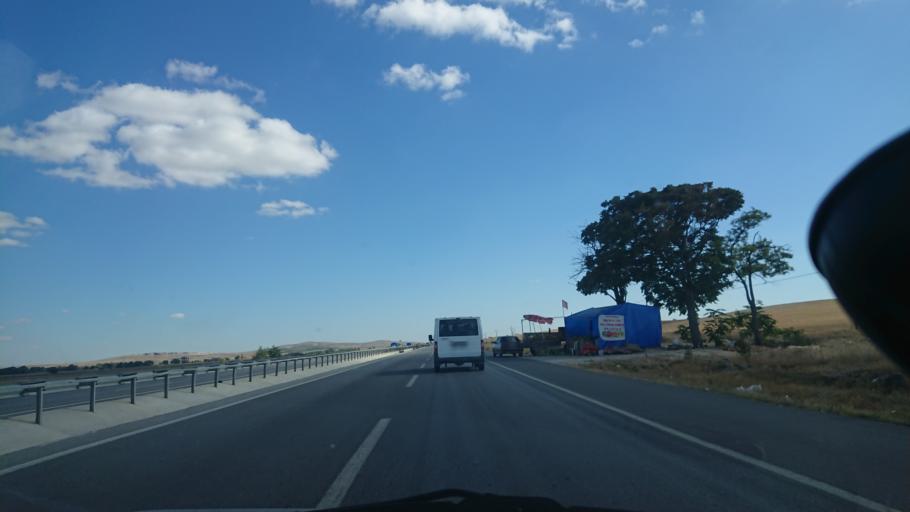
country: TR
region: Eskisehir
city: Mahmudiye
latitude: 39.5266
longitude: 30.9533
